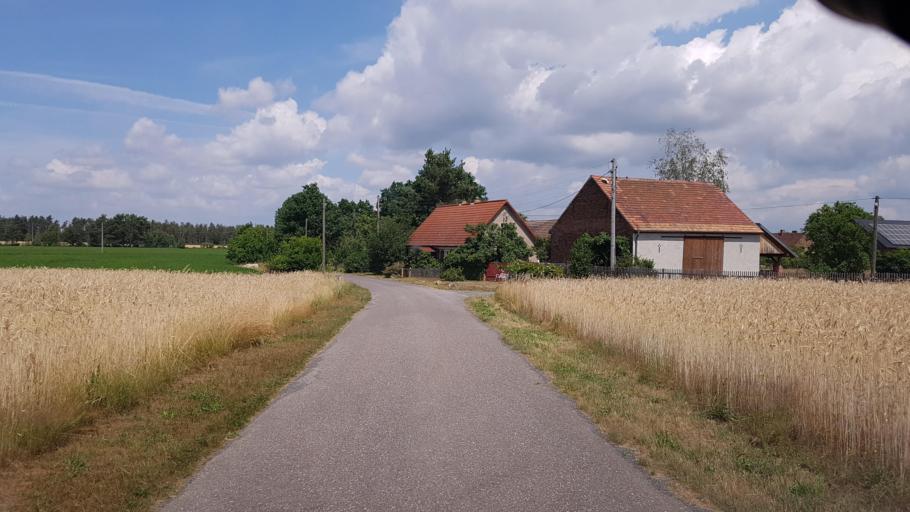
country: DE
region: Brandenburg
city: Crinitz
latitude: 51.7467
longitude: 13.8300
